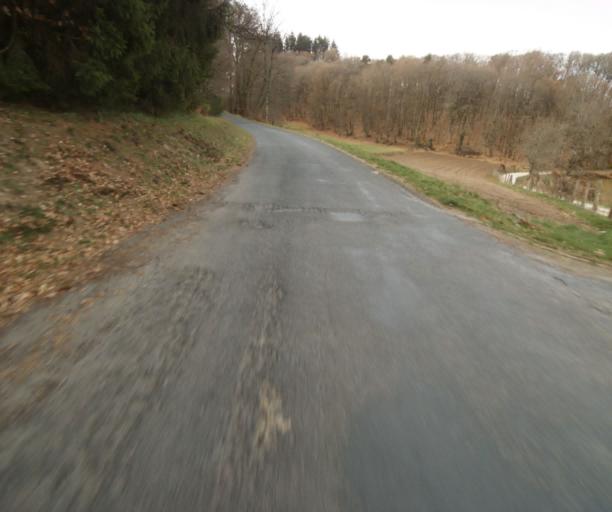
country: FR
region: Limousin
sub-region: Departement de la Correze
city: Treignac
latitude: 45.4493
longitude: 1.8189
